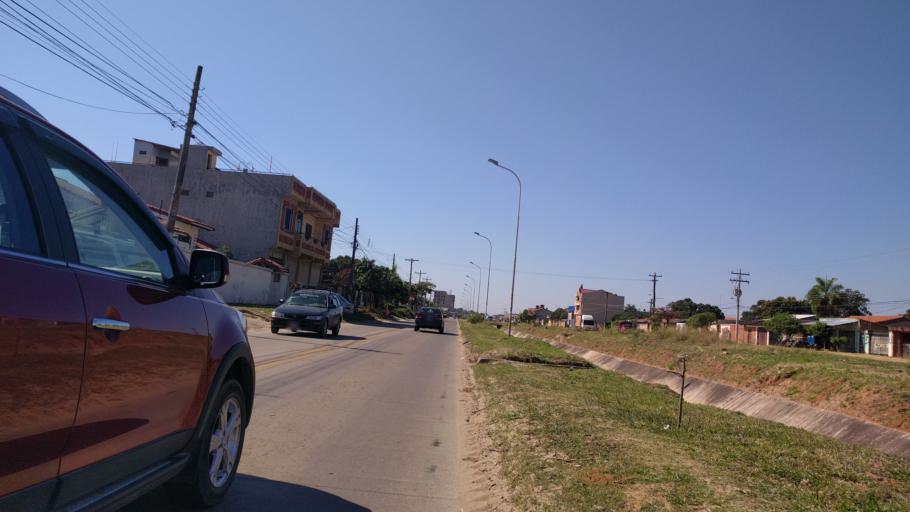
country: BO
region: Santa Cruz
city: Santa Cruz de la Sierra
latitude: -17.8436
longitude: -63.1859
